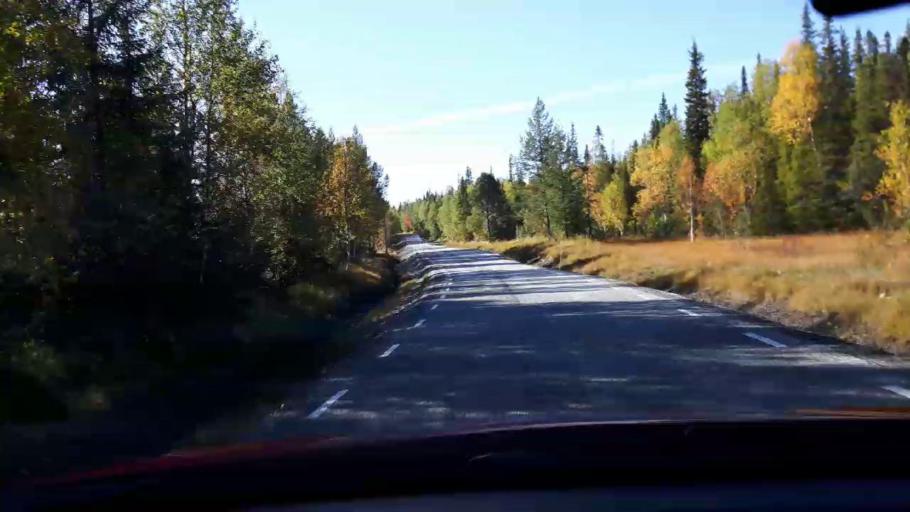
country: NO
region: Nord-Trondelag
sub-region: Royrvik
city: Royrvik
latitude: 64.8167
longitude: 14.2144
